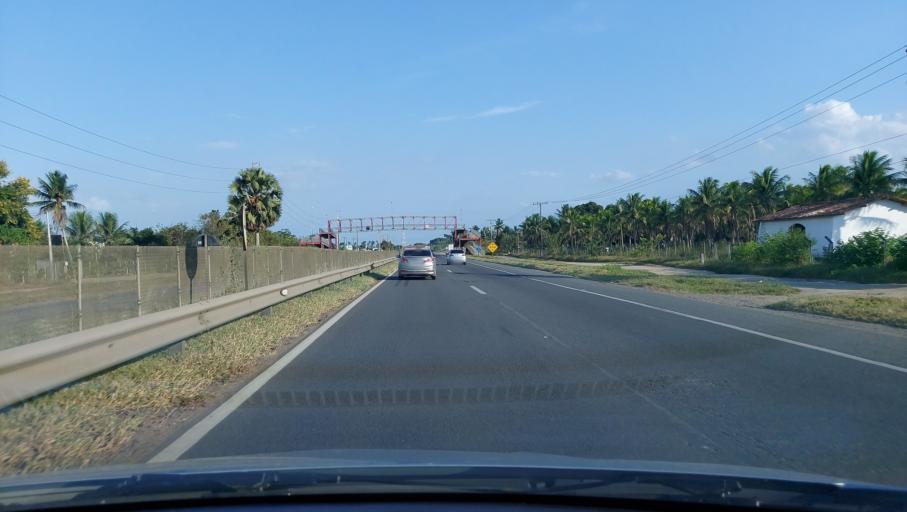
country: BR
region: Bahia
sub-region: Conceicao Do Jacuipe
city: Conceicao do Jacuipe
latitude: -12.3824
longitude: -38.7963
